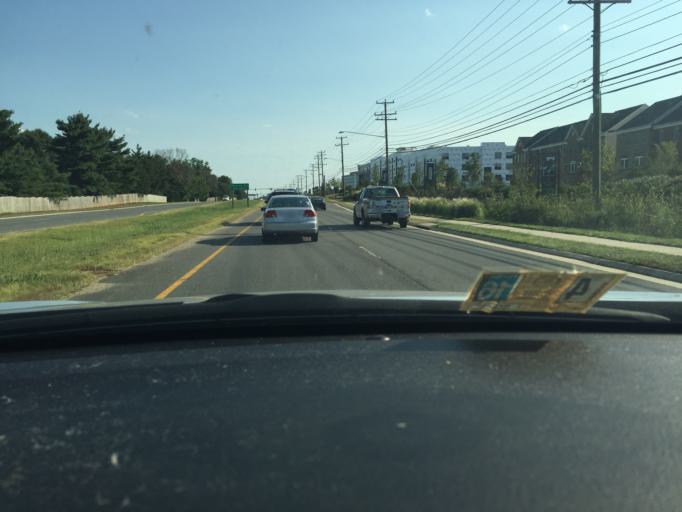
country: US
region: Virginia
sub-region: Fairfax County
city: Floris
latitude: 38.9204
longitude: -77.4183
